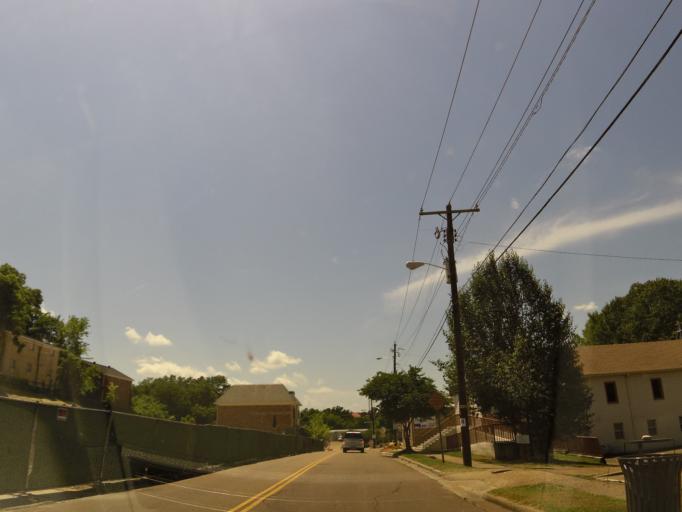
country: US
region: Mississippi
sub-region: Lafayette County
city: University
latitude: 34.3676
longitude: -89.5245
